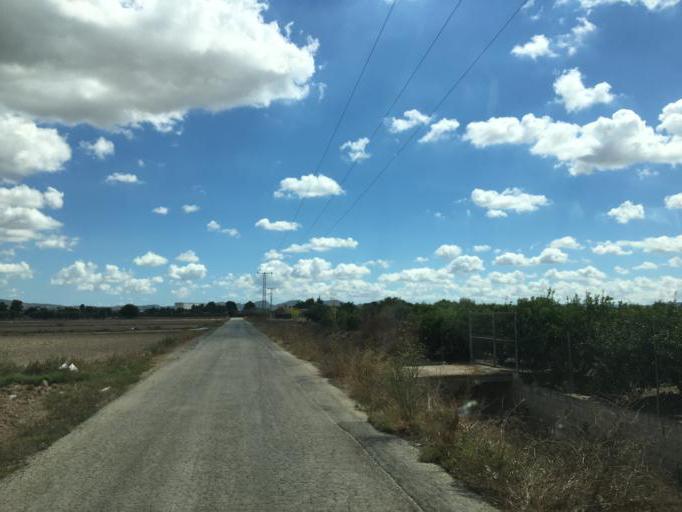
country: ES
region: Murcia
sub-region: Murcia
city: Santomera
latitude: 38.0479
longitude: -1.0451
